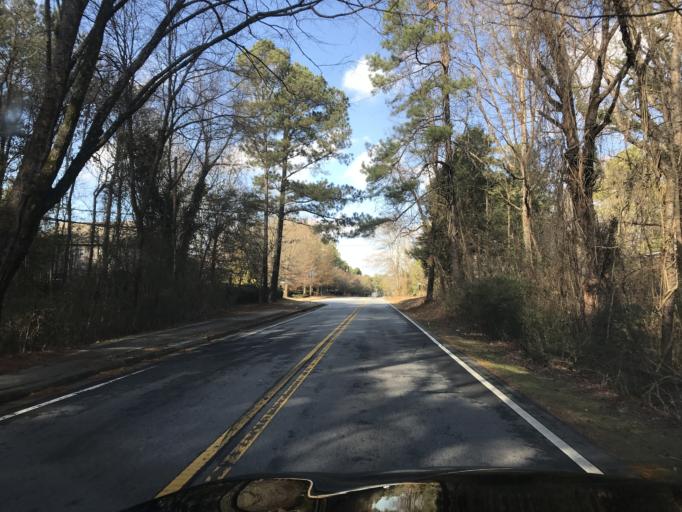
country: US
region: Georgia
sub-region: Cobb County
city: Mableton
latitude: 33.7138
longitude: -84.5593
